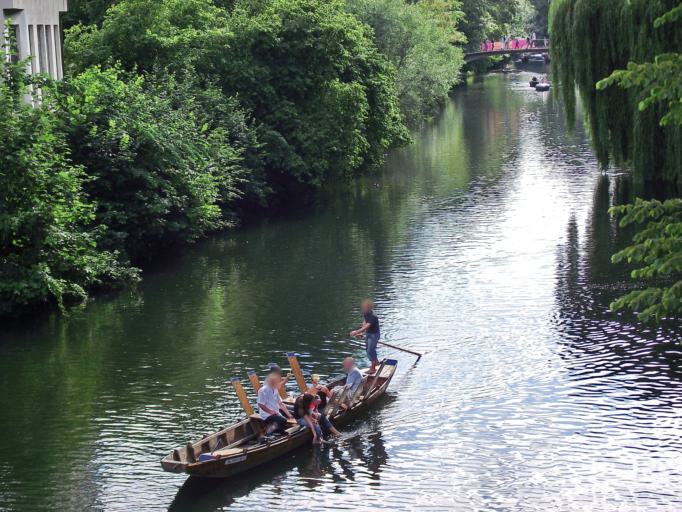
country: DE
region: Baden-Wuerttemberg
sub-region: Tuebingen Region
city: Tuebingen
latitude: 48.5189
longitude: 9.0581
